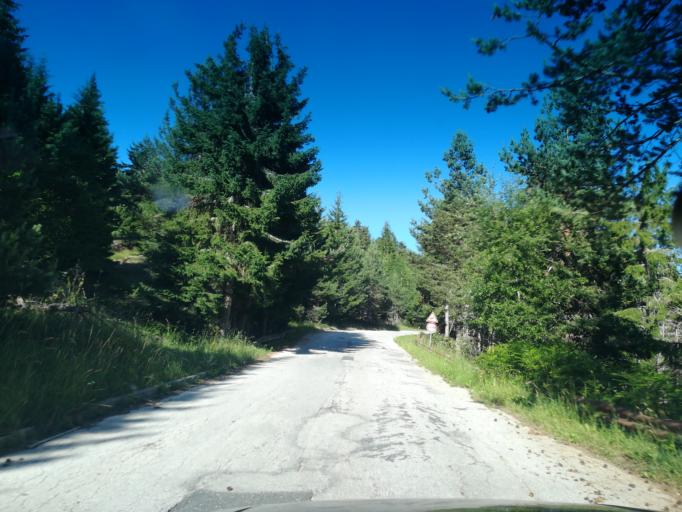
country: BG
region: Smolyan
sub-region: Obshtina Chepelare
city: Chepelare
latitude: 41.6923
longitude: 24.7626
